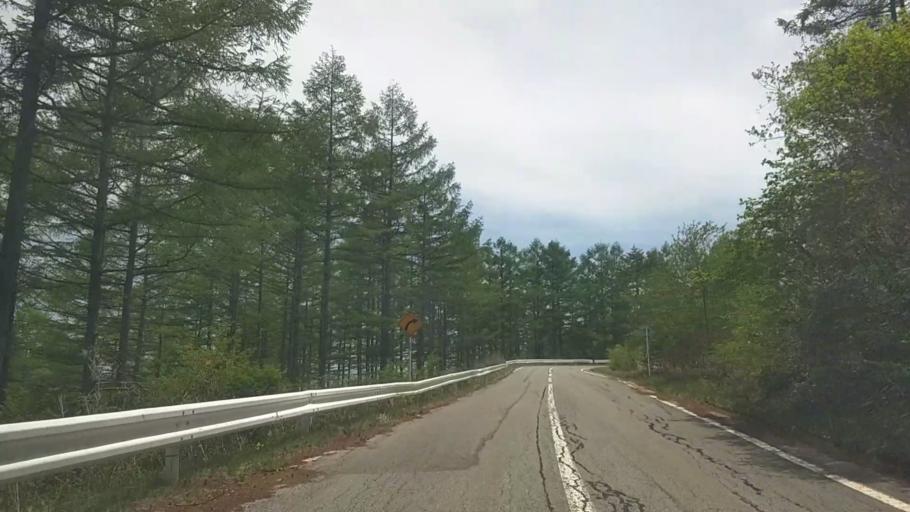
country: JP
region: Nagano
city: Saku
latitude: 36.0921
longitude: 138.3904
